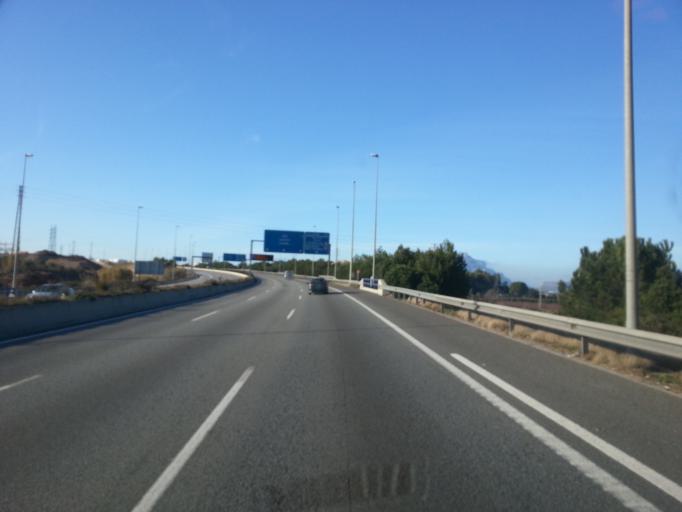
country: ES
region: Catalonia
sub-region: Provincia de Barcelona
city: Martorell
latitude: 41.4970
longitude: 1.9197
